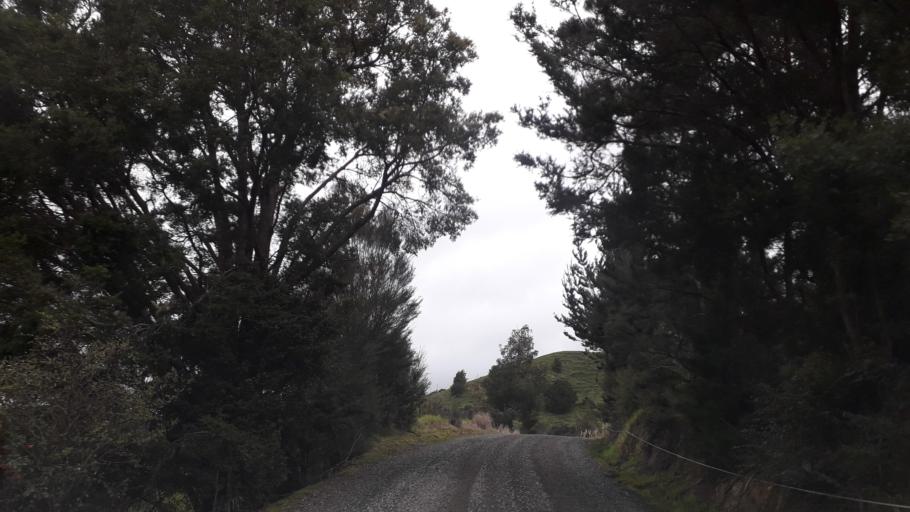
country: NZ
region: Northland
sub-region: Far North District
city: Waimate North
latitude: -35.1472
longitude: 173.7122
